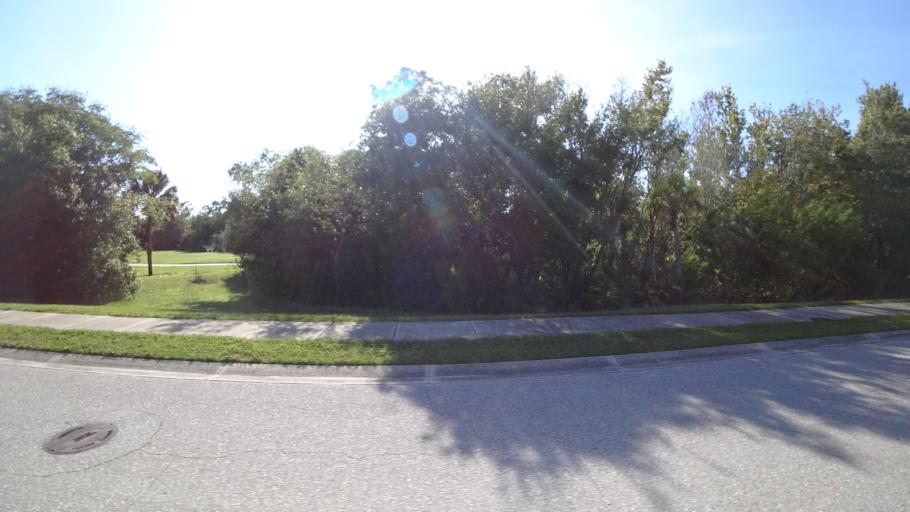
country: US
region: Florida
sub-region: Sarasota County
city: Desoto Lakes
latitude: 27.4311
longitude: -82.4620
